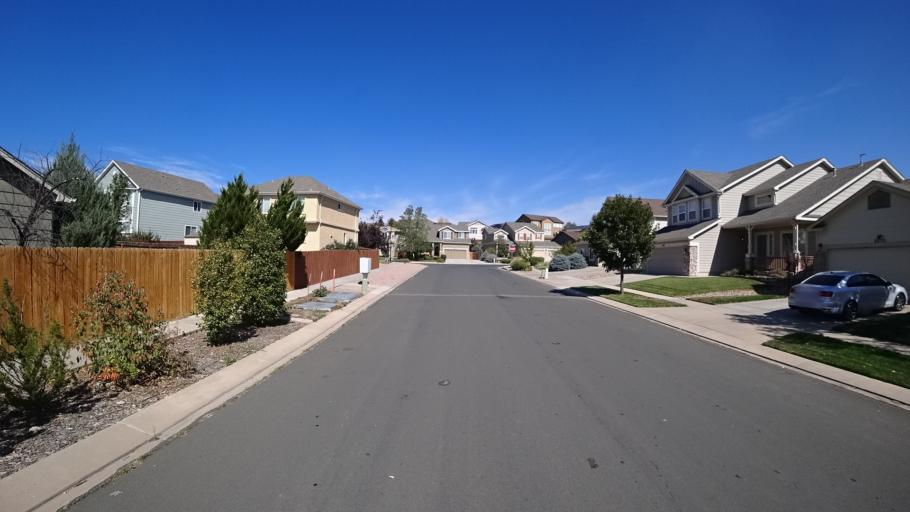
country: US
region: Colorado
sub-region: El Paso County
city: Cimarron Hills
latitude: 38.8983
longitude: -104.6921
